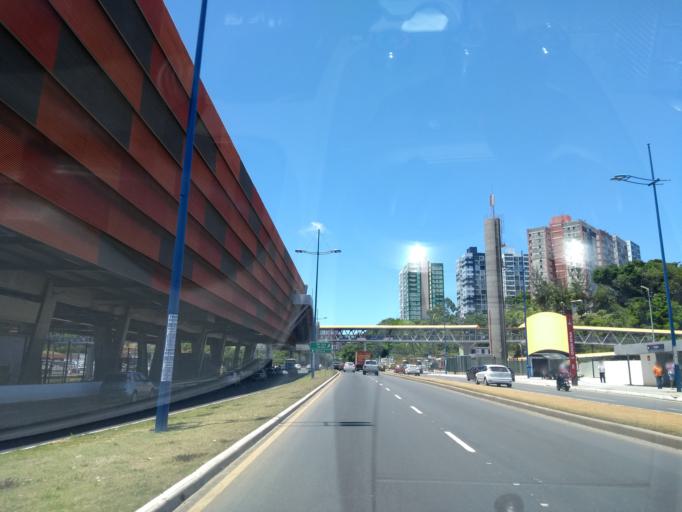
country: BR
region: Bahia
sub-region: Salvador
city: Salvador
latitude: -12.9780
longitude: -38.4706
